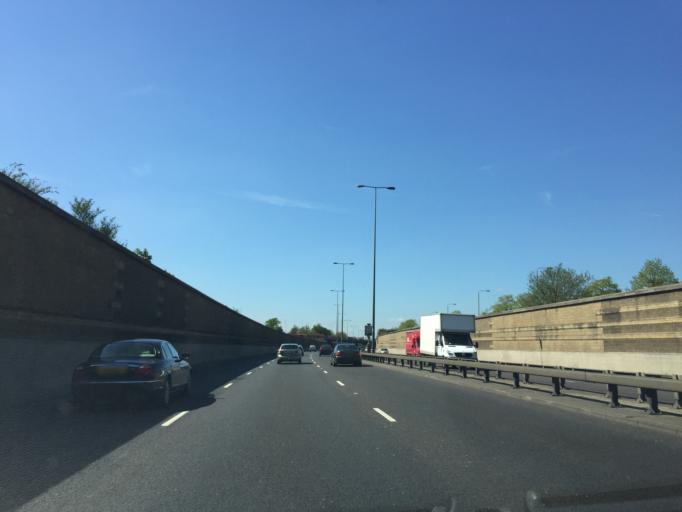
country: GB
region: England
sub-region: Greater London
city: Walthamstow
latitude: 51.5633
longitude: 0.0039
